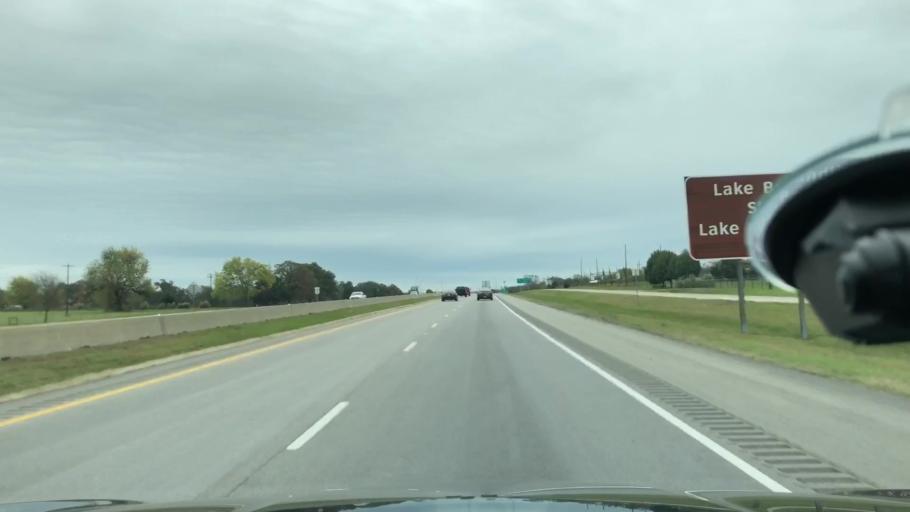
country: US
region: Texas
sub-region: Franklin County
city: Mount Vernon
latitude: 33.1628
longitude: -95.2484
